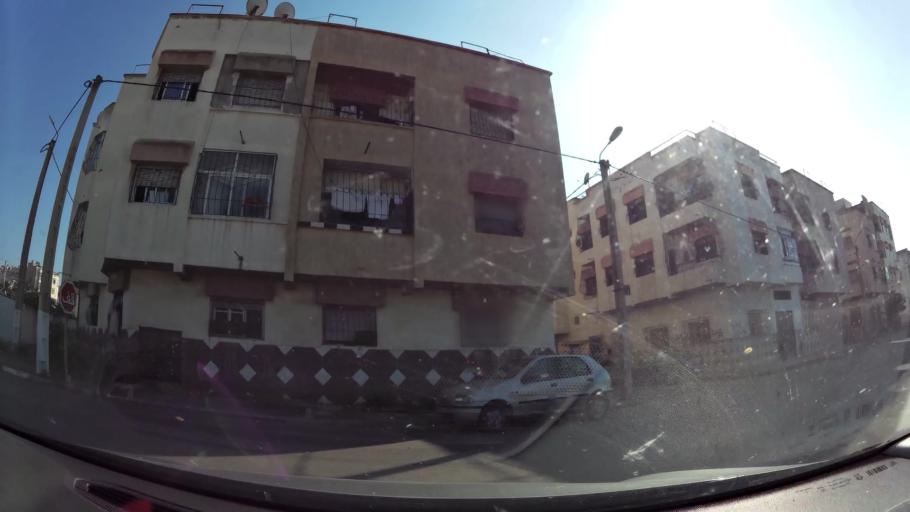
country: MA
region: Rabat-Sale-Zemmour-Zaer
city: Sale
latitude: 34.0478
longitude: -6.8099
